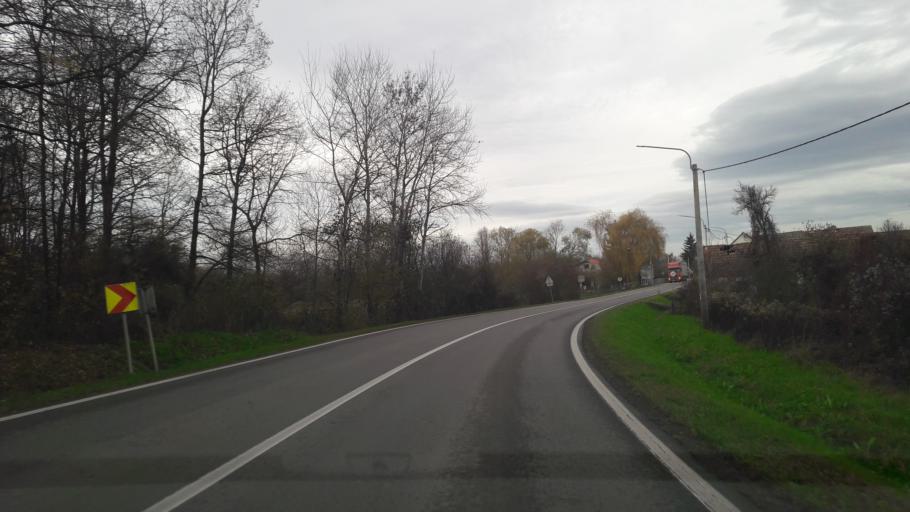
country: HR
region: Osjecko-Baranjska
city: Fericanci
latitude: 45.5211
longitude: 18.0004
